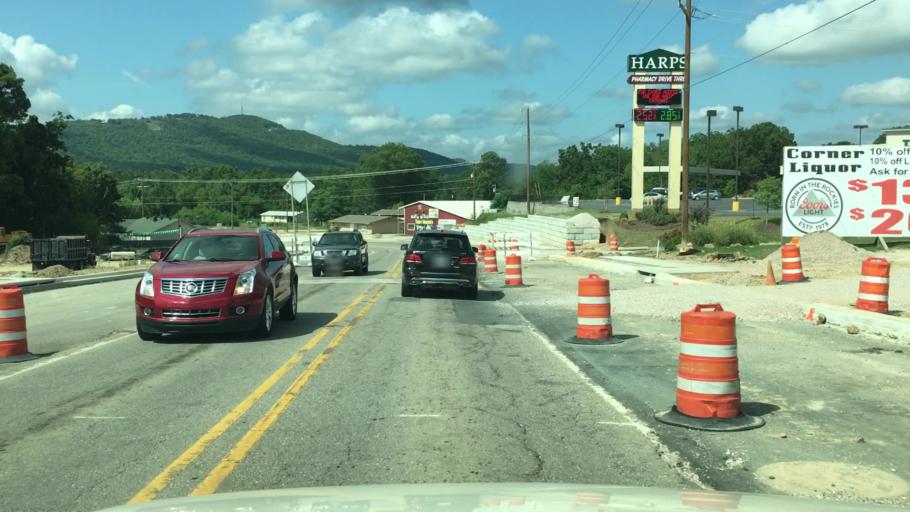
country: US
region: Arkansas
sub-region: Garland County
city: Lake Hamilton
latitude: 34.4241
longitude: -93.0960
